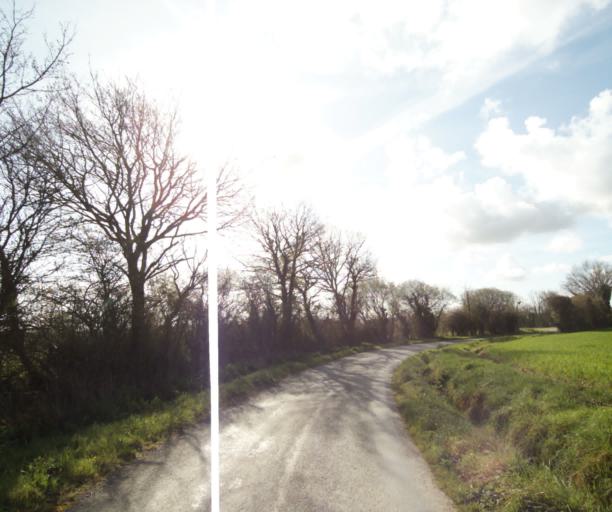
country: FR
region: Pays de la Loire
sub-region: Departement de la Loire-Atlantique
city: Bouvron
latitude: 47.4015
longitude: -1.8363
